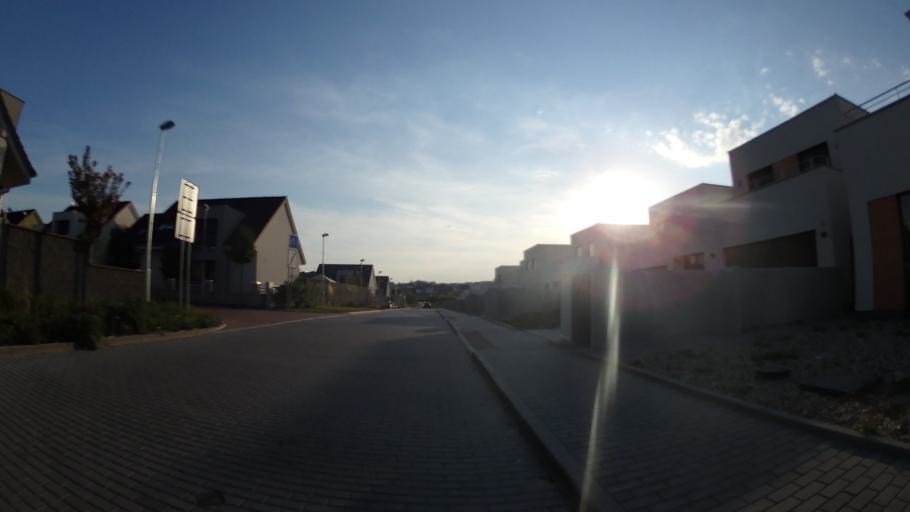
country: CZ
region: South Moravian
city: Moravany
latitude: 49.1520
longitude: 16.5826
